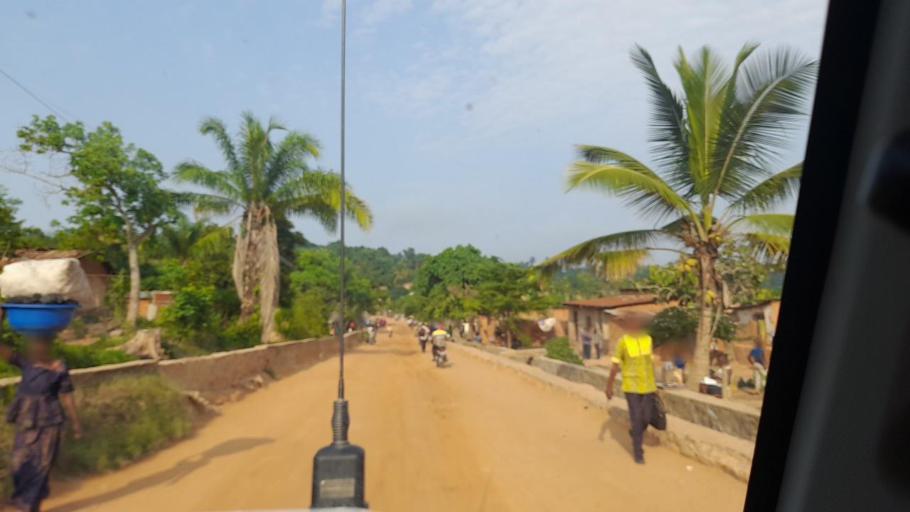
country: CD
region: Kasai-Occidental
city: Kananga
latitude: -5.8947
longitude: 22.3826
